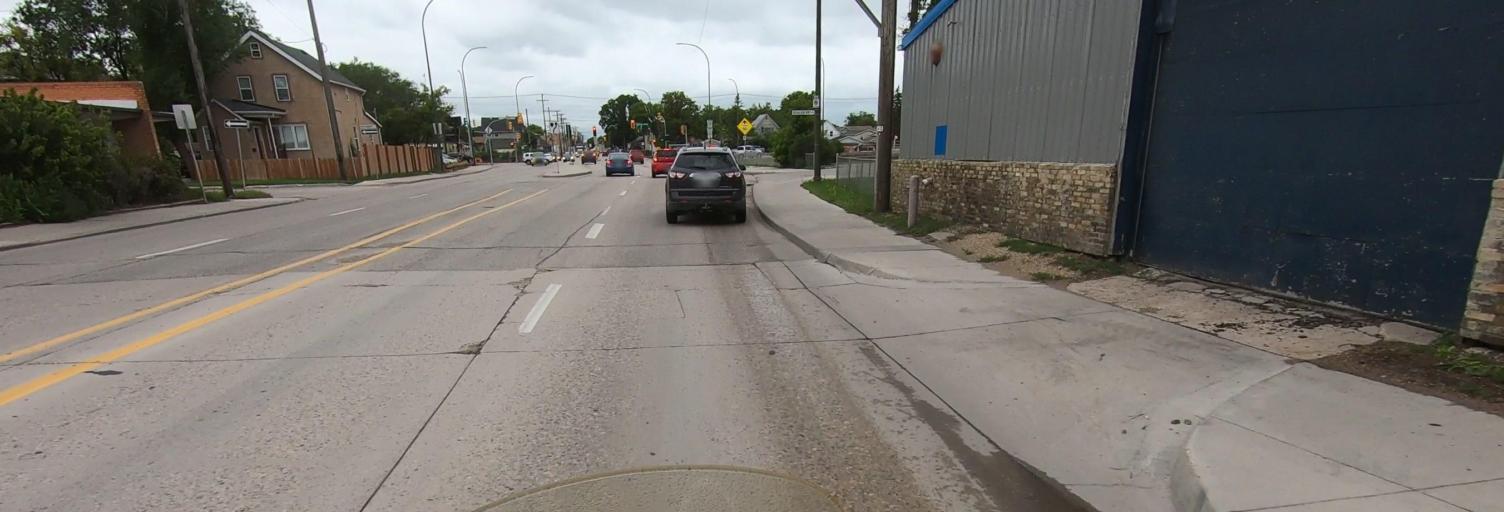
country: CA
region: Manitoba
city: Winnipeg
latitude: 49.9037
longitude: -97.1056
